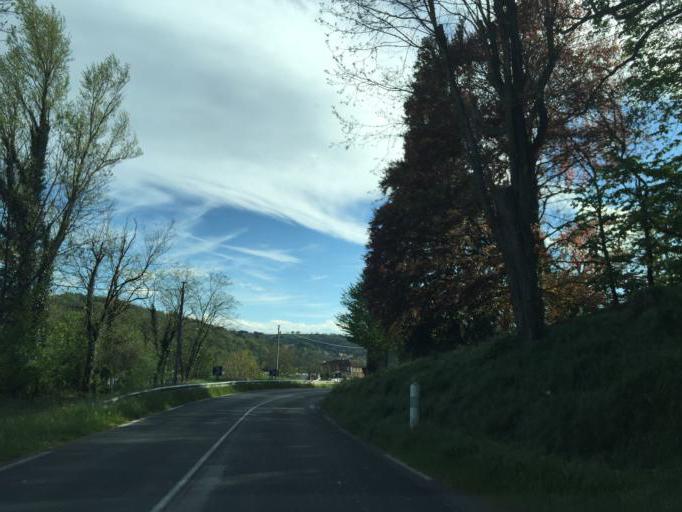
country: FR
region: Rhone-Alpes
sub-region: Departement du Rhone
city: Echalas
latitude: 45.5758
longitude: 4.7181
